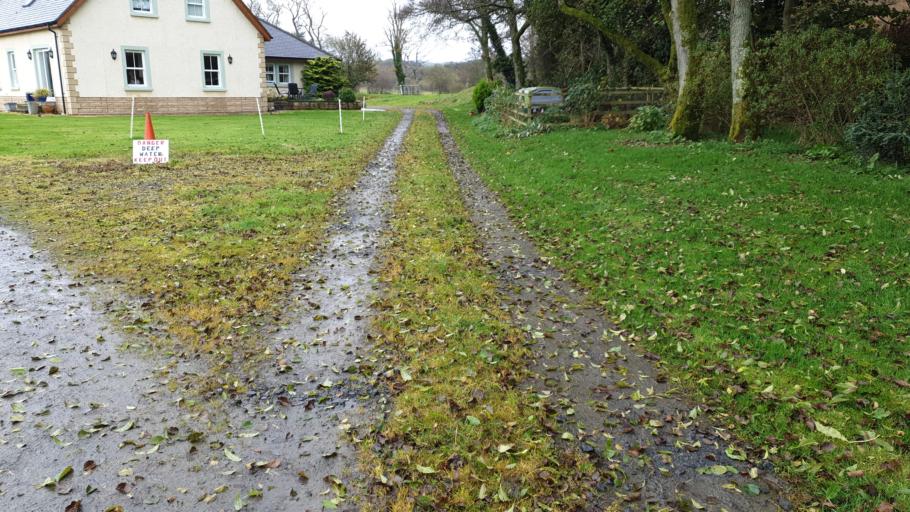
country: GB
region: Scotland
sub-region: East Ayrshire
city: Dalrymple
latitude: 55.3953
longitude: -4.5868
